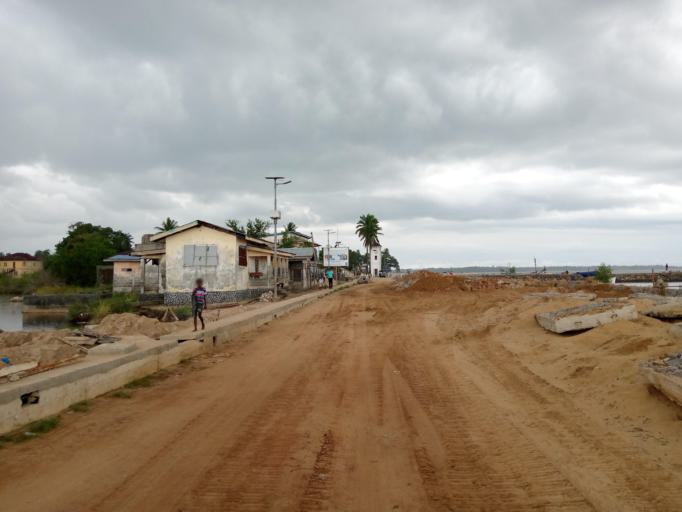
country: SL
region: Southern Province
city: Bonthe
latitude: 7.5294
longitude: -12.5009
